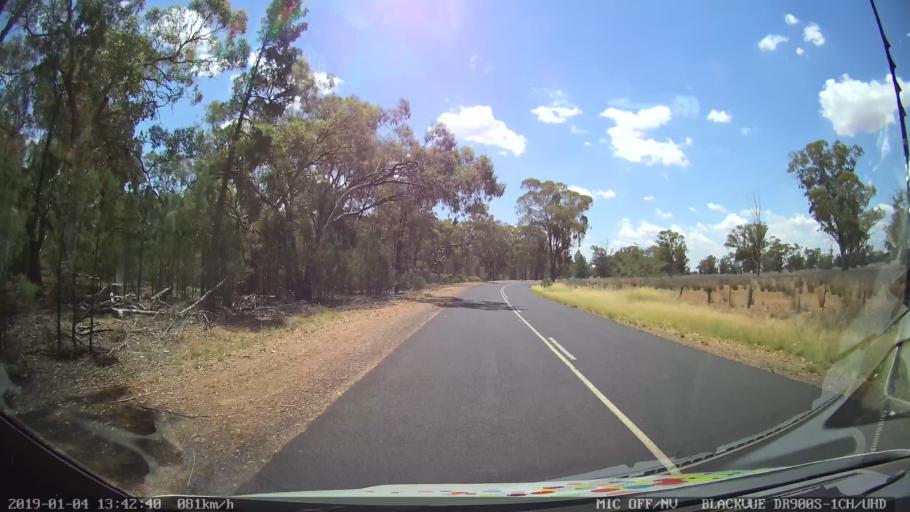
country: AU
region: New South Wales
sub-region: Dubbo Municipality
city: Dubbo
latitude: -32.4870
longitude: 148.5561
